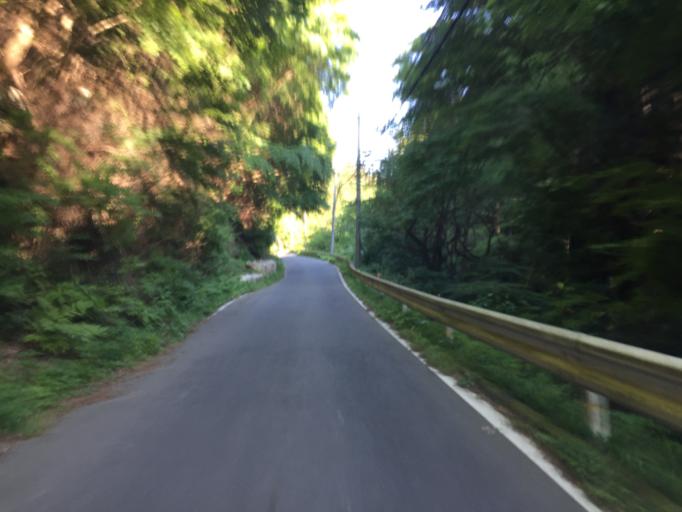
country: JP
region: Ibaraki
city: Kitaibaraki
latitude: 36.8681
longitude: 140.6586
